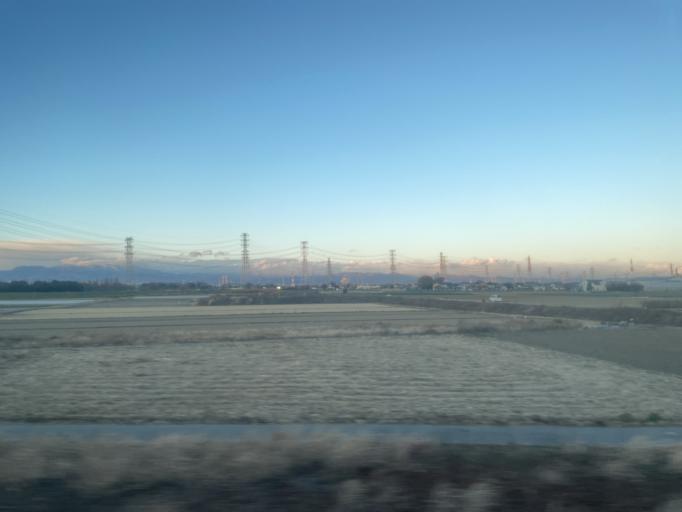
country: JP
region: Saitama
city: Honjo
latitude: 36.2162
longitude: 139.2173
